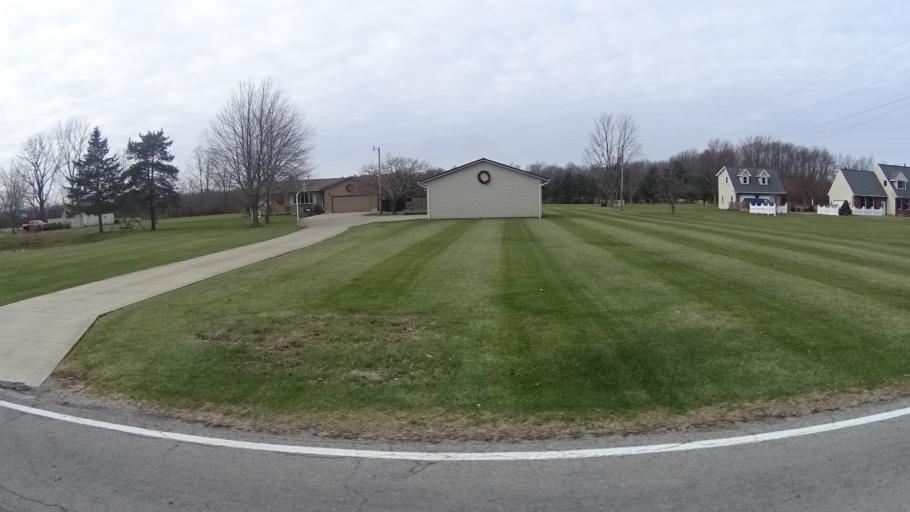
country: US
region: Ohio
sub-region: Lorain County
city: Wellington
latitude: 41.1912
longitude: -82.2686
